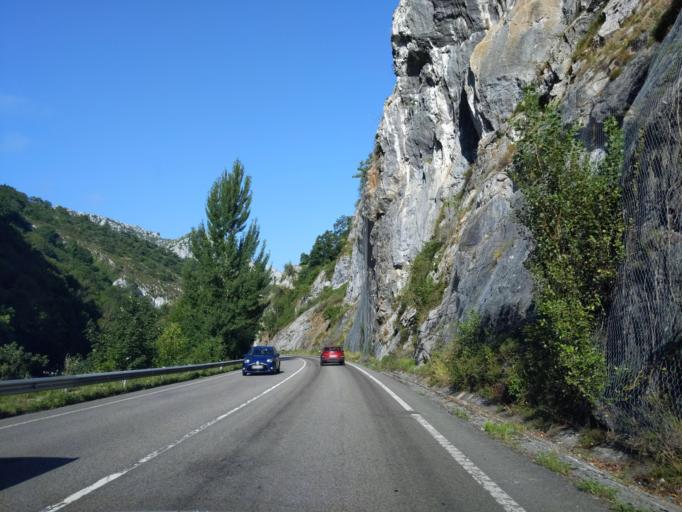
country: ES
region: Asturias
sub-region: Province of Asturias
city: Pola de Laviana
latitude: 43.2320
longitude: -5.4893
